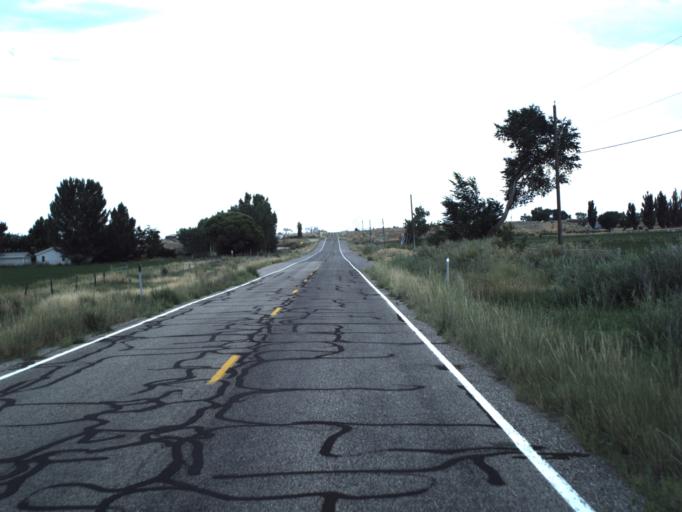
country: US
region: Utah
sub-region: Emery County
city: Huntington
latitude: 39.4006
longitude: -110.8526
